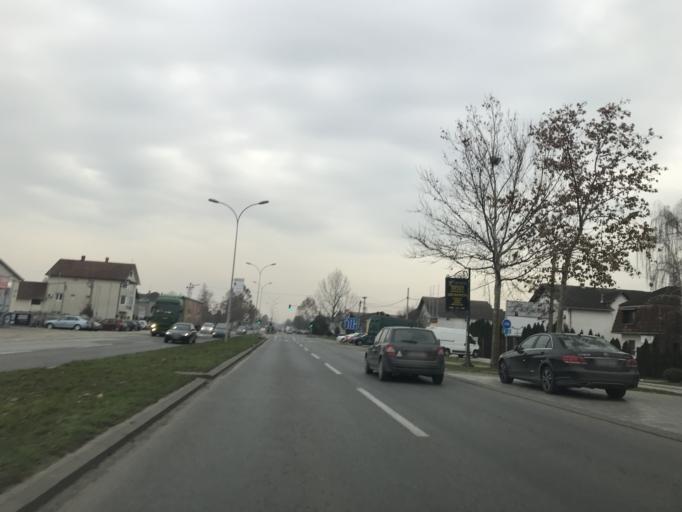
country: RS
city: Veternik
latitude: 45.2472
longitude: 19.7659
